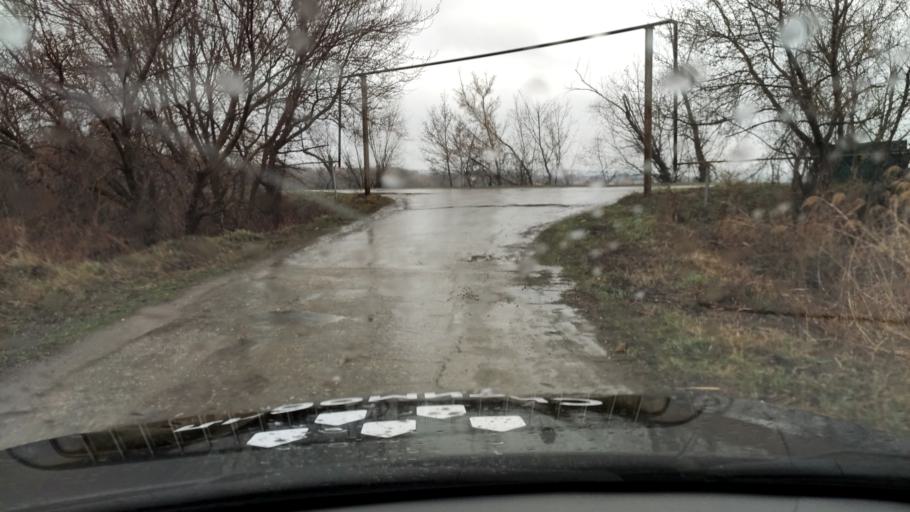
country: RU
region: Samara
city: Balasheyka
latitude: 53.2310
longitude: 48.2380
